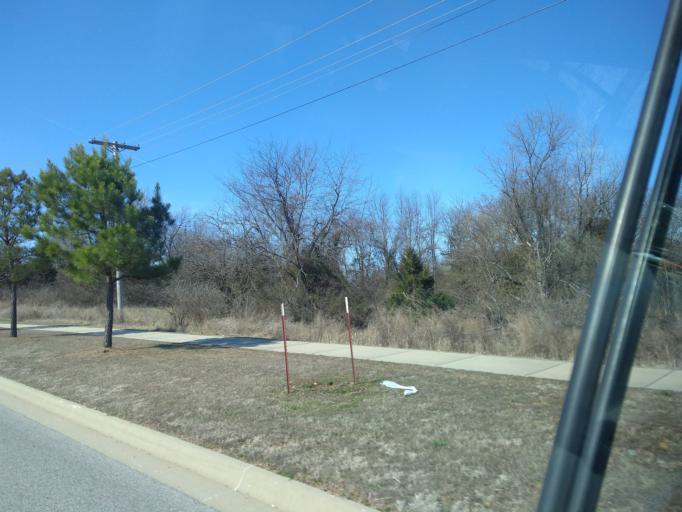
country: US
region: Arkansas
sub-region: Washington County
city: Farmington
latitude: 36.0593
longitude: -94.2347
